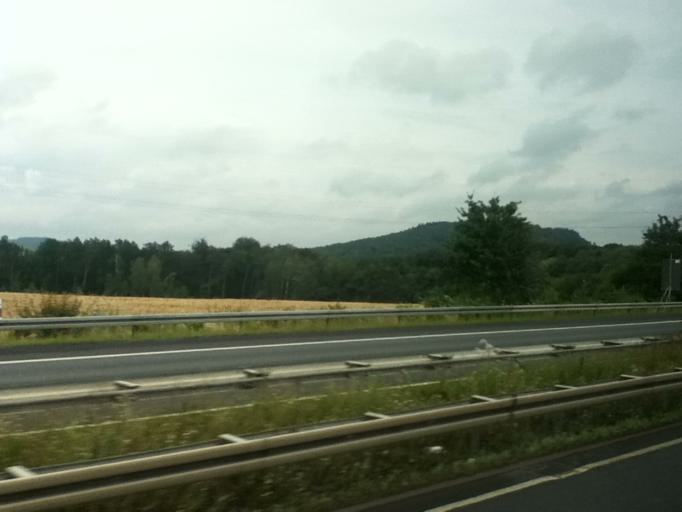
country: DE
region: Hesse
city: Lollar
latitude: 50.6263
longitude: 8.7054
